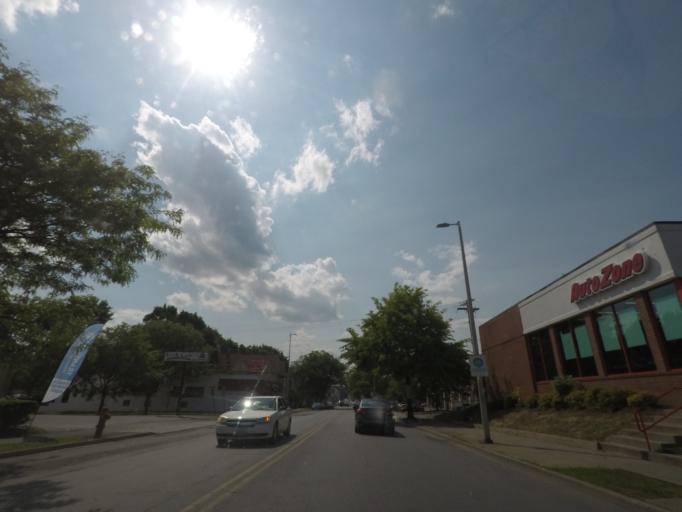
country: US
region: New York
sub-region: Dutchess County
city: Arlington
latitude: 41.6971
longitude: -73.9067
